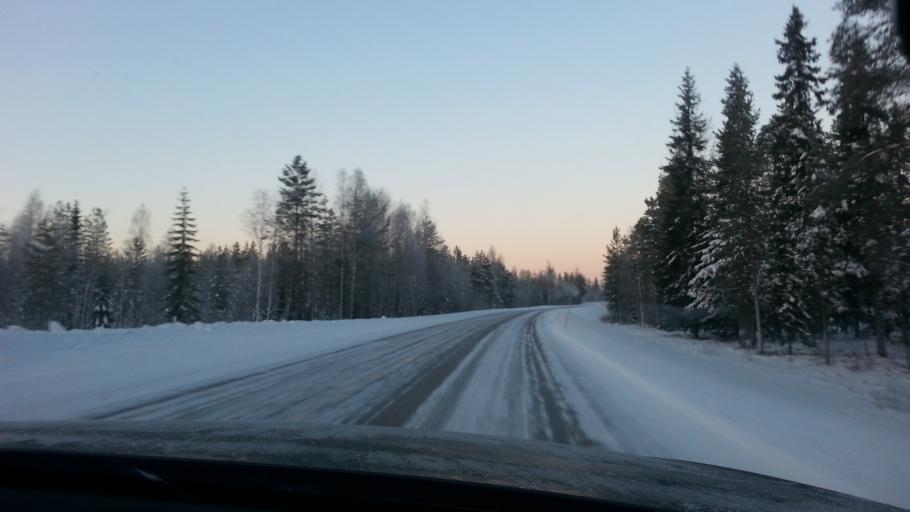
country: FI
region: Lapland
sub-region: Rovaniemi
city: Rovaniemi
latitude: 66.7799
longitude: 25.4481
